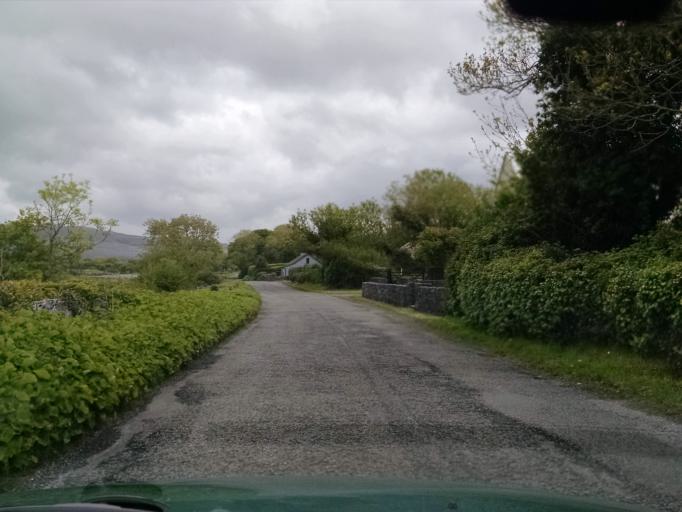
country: IE
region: Connaught
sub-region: County Galway
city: Bearna
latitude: 53.1224
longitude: -9.1647
